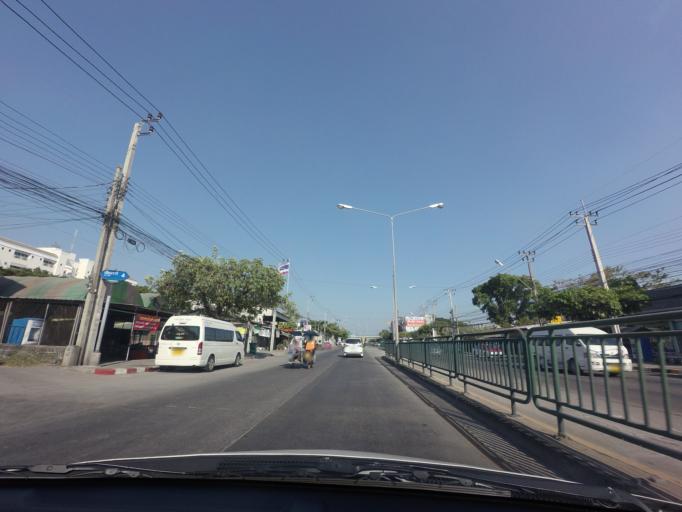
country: TH
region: Bangkok
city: Nong Chok
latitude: 13.8559
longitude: 100.8582
